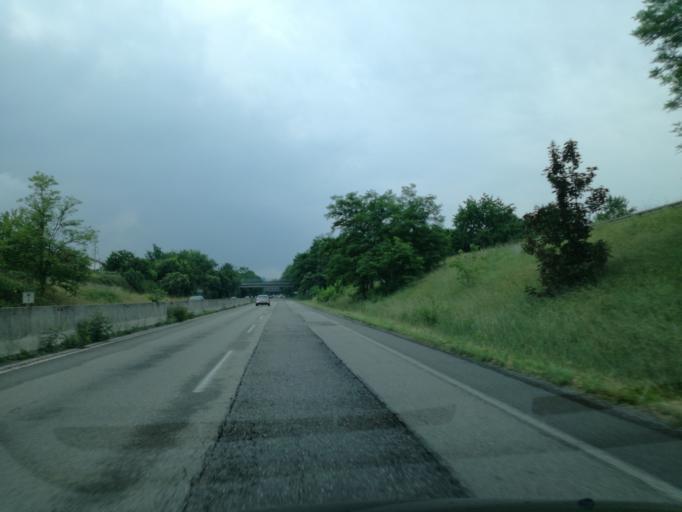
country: IT
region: Lombardy
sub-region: Provincia di Monza e Brianza
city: Villasanta
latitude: 45.5983
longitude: 9.3161
